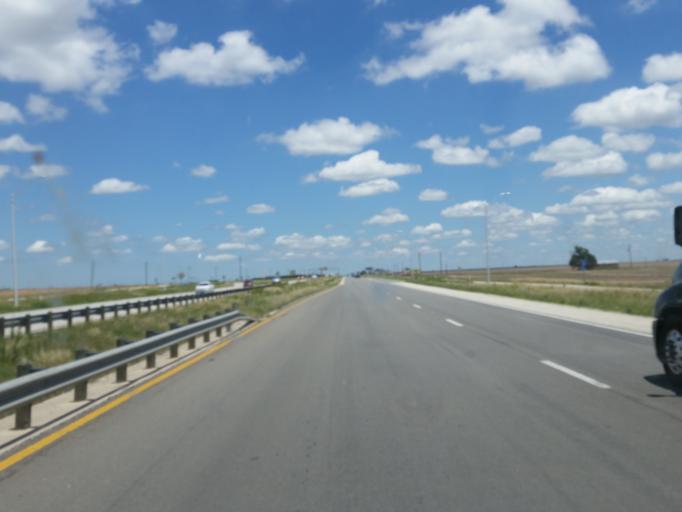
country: US
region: Texas
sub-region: Nolan County
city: Roscoe
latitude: 32.4472
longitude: -100.5008
